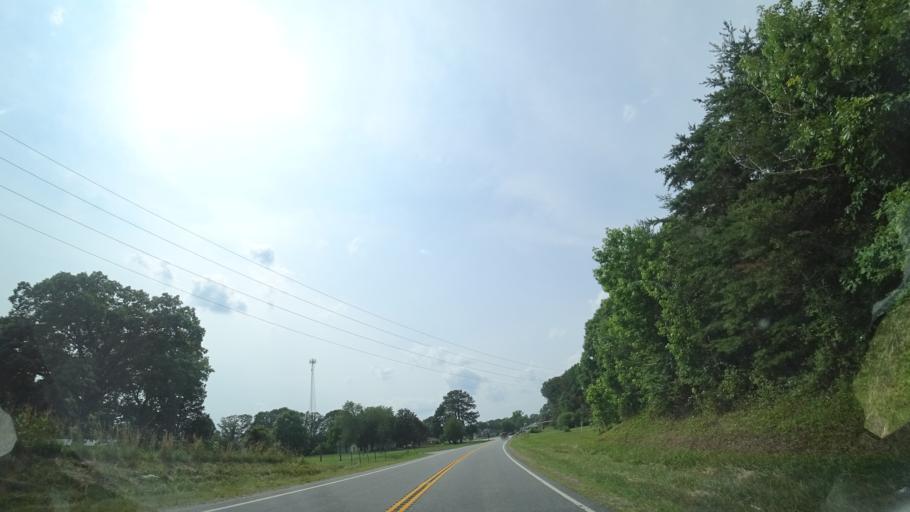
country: US
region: Virginia
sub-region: Spotsylvania County
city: Spotsylvania Courthouse
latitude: 38.1159
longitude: -77.7565
